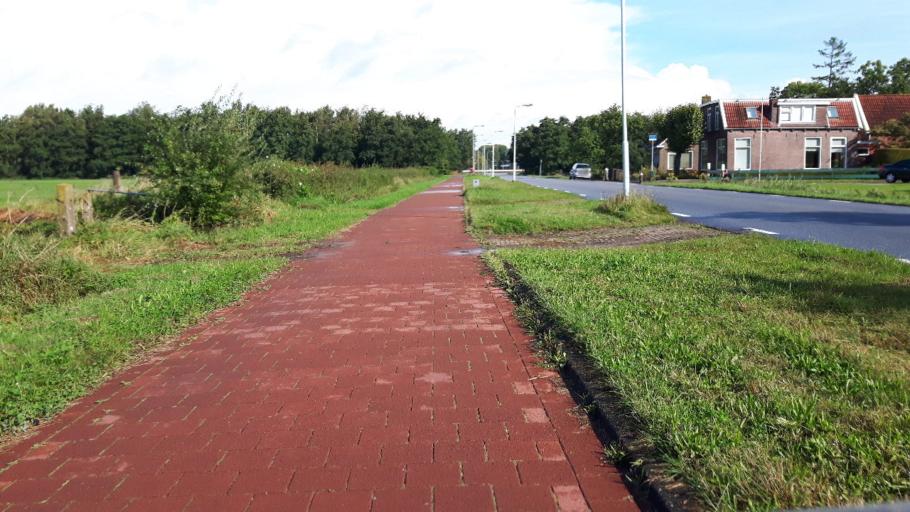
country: NL
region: Friesland
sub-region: Gemeente Smallingerland
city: Drachten
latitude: 53.0900
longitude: 6.0995
